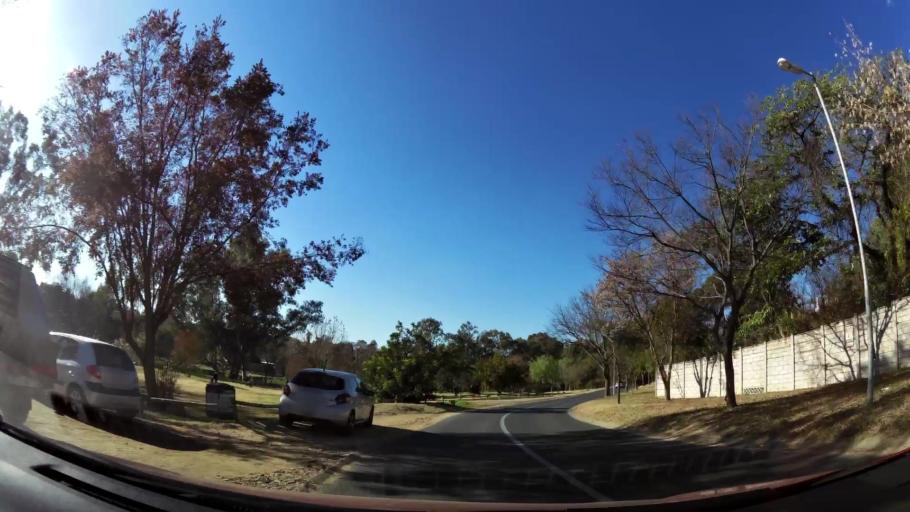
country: ZA
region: Gauteng
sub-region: City of Johannesburg Metropolitan Municipality
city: Diepsloot
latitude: -26.0447
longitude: 27.9857
